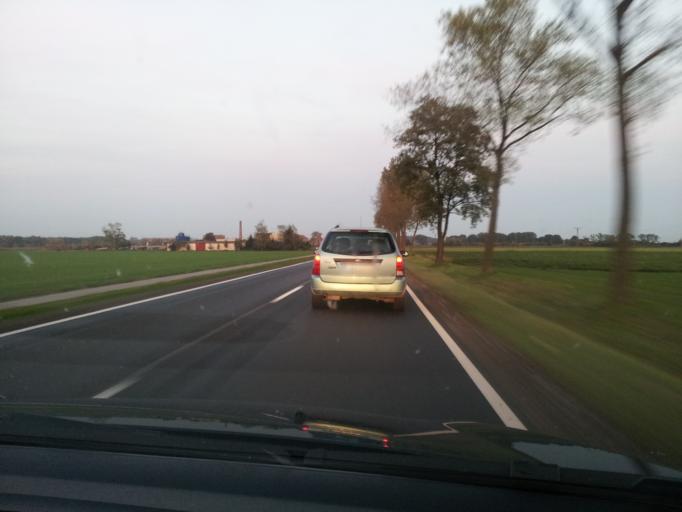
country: PL
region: Kujawsko-Pomorskie
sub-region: Powiat inowroclawski
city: Gniewkowo
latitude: 52.9012
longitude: 18.4393
